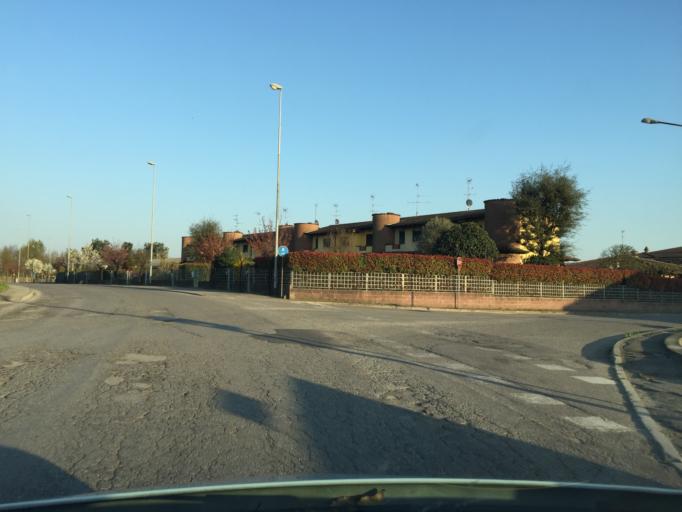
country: IT
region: Lombardy
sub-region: Provincia di Brescia
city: Pralboino
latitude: 45.2642
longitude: 10.2187
